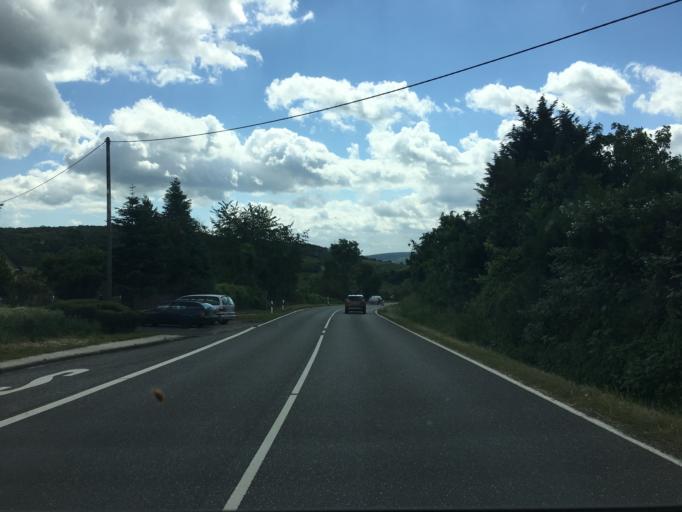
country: DE
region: Rheinland-Pfalz
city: Bad Neuenahr-Ahrweiler
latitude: 50.5590
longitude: 7.1088
